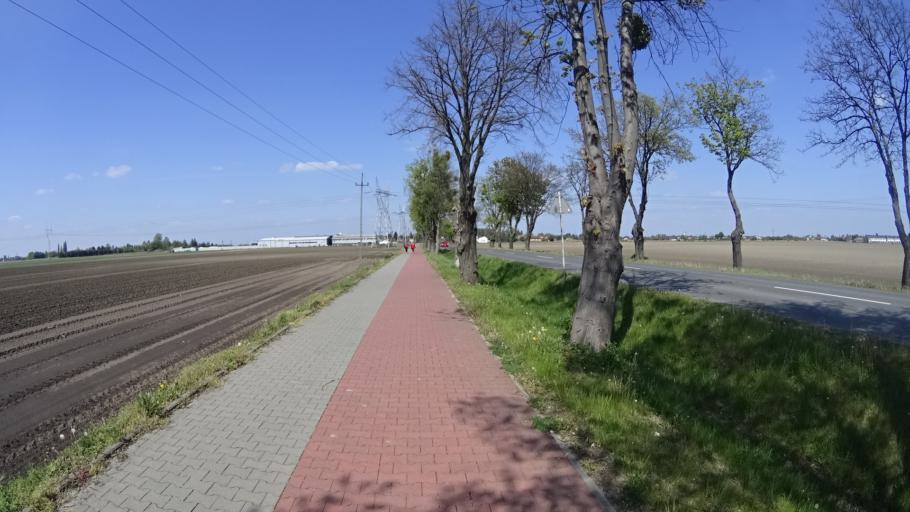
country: PL
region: Masovian Voivodeship
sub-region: Powiat warszawski zachodni
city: Stare Babice
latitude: 52.2361
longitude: 20.8165
